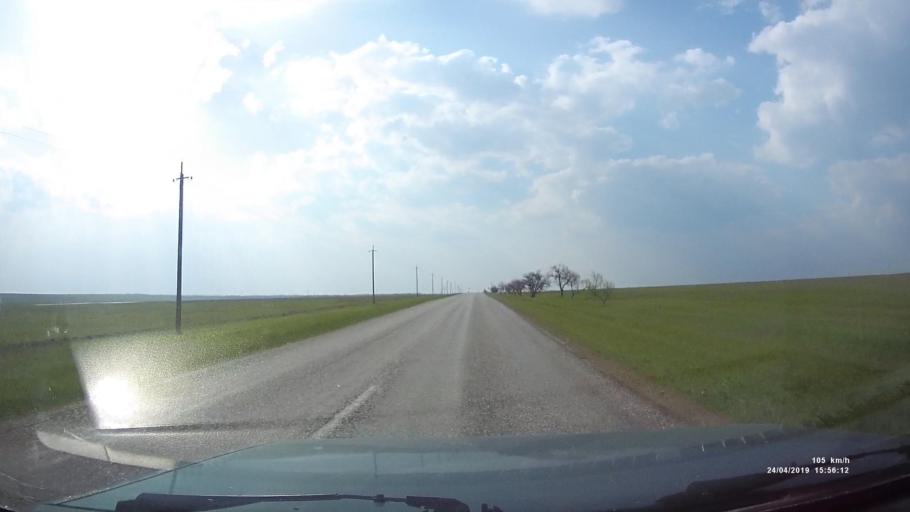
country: RU
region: Kalmykiya
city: Yashalta
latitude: 46.5960
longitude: 42.5335
